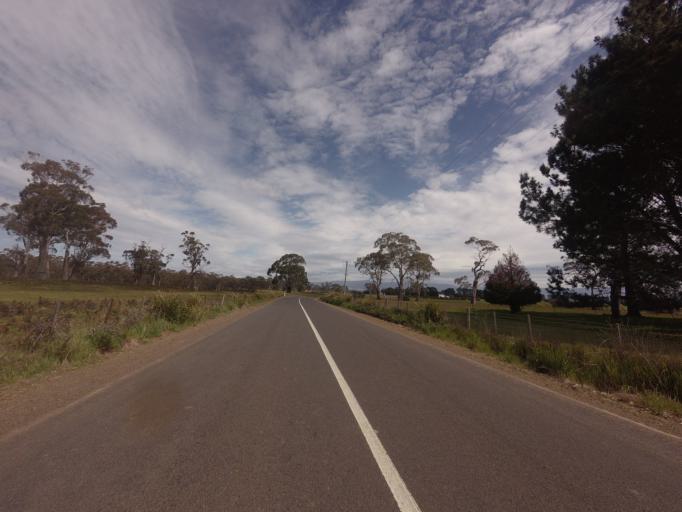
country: AU
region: Tasmania
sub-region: Northern Midlands
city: Longford
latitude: -41.7135
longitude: 147.1937
